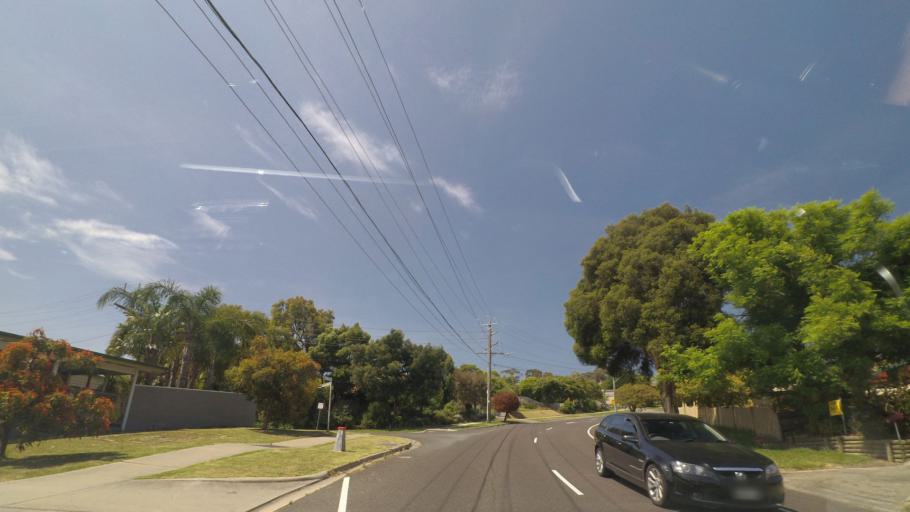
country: AU
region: Victoria
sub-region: Yarra Ranges
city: Chirnside Park
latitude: -37.7521
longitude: 145.3149
